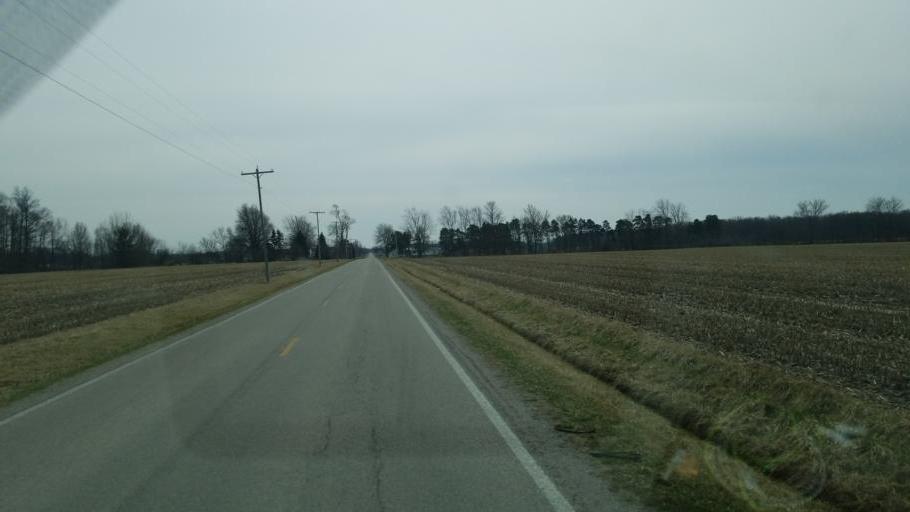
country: US
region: Ohio
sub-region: Huron County
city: Wakeman
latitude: 41.1999
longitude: -82.4908
